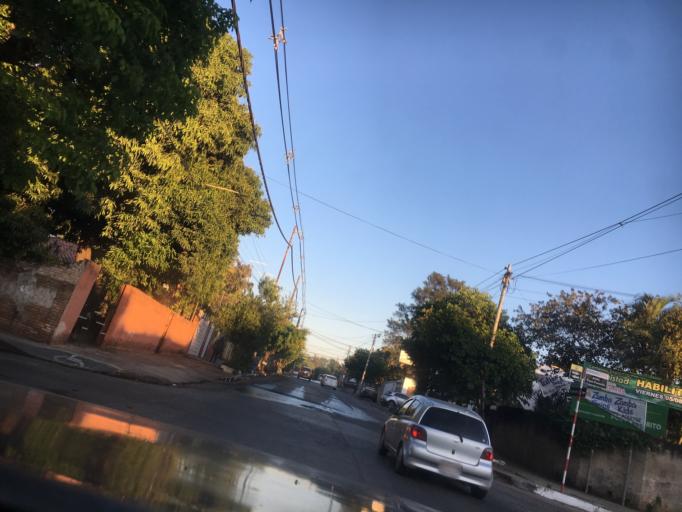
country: PY
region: Asuncion
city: Asuncion
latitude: -25.3098
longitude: -57.6270
